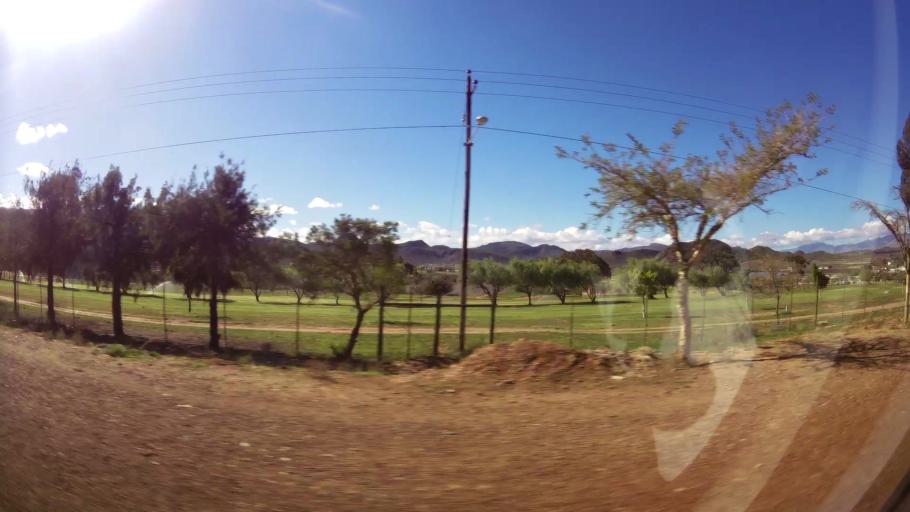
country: ZA
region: Western Cape
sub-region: Cape Winelands District Municipality
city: Ashton
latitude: -33.7723
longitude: 20.1319
